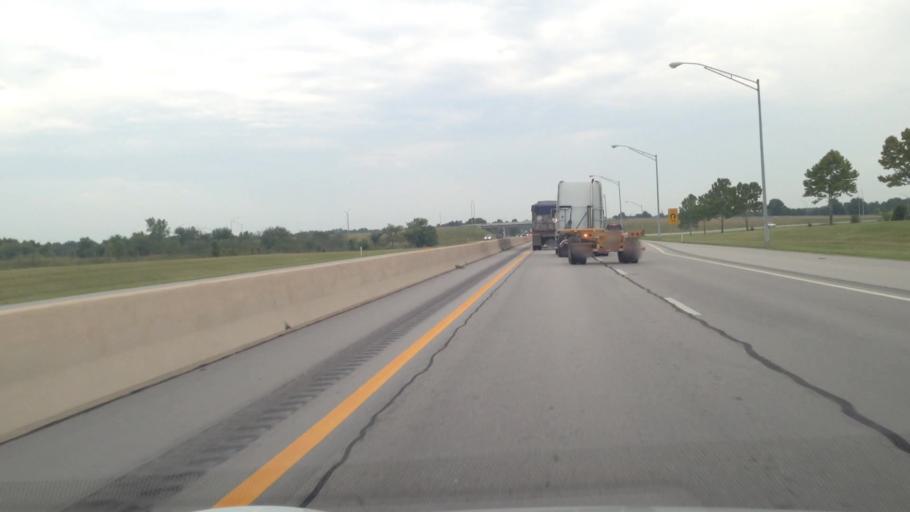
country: US
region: Oklahoma
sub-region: Ottawa County
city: Miami
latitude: 36.8695
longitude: -94.8481
